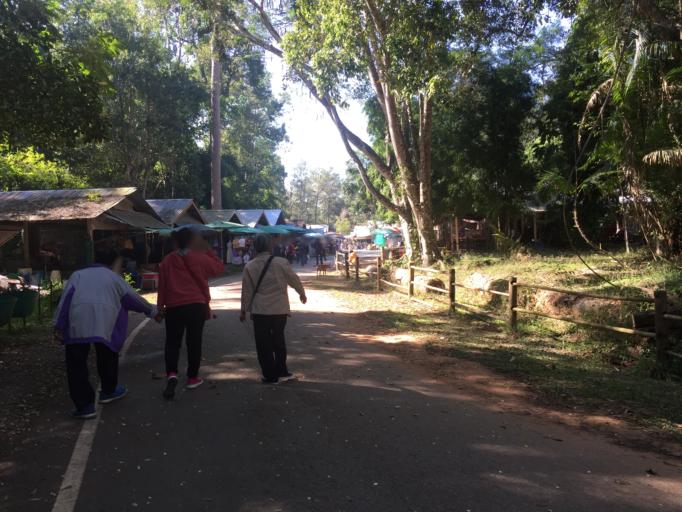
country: TH
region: Phetchabun
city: Khao Kho
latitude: 16.6290
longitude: 100.9403
